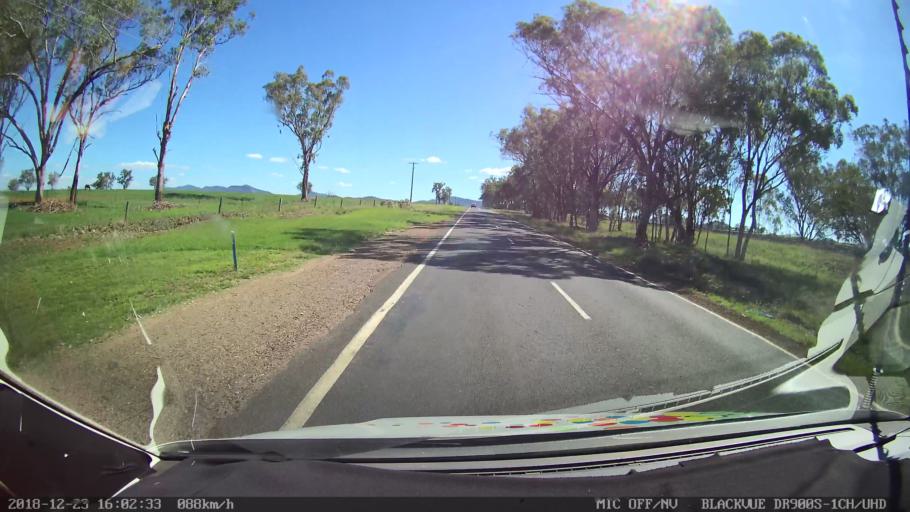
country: AU
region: New South Wales
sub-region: Tamworth Municipality
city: Phillip
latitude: -31.2335
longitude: 150.8081
